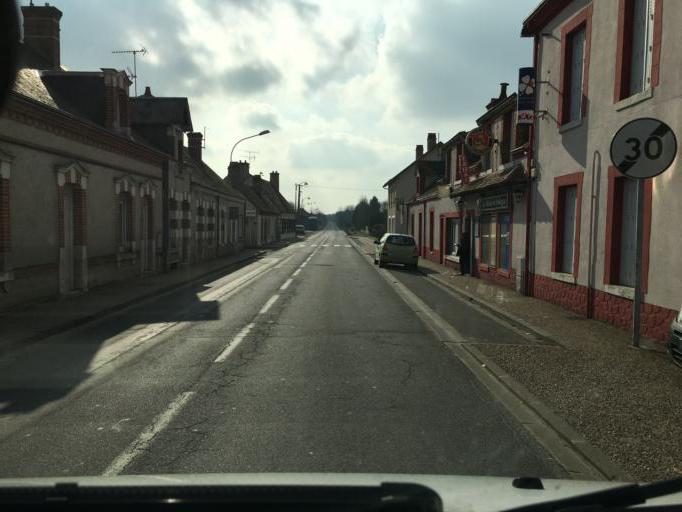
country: FR
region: Centre
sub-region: Departement du Loir-et-Cher
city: Romorantin-Lanthenay
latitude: 47.4468
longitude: 1.7718
